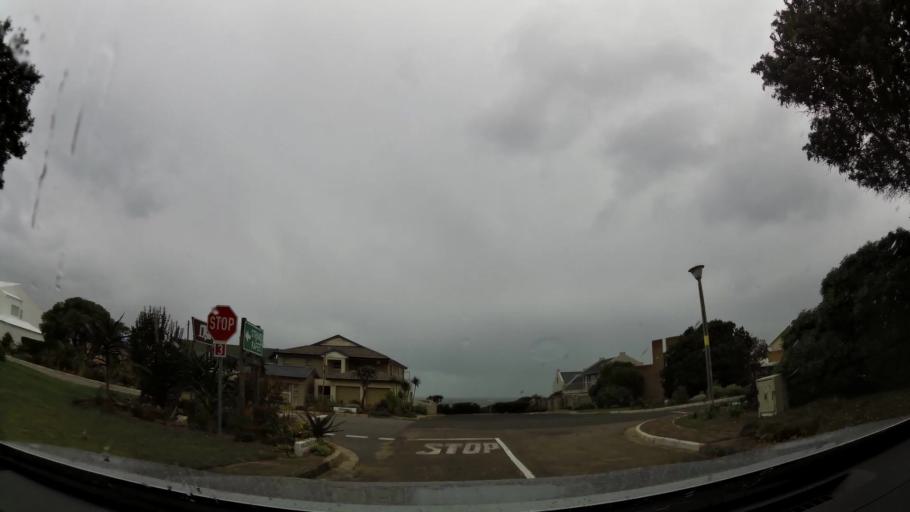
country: ZA
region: Western Cape
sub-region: Eden District Municipality
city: George
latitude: -34.0496
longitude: 22.3071
